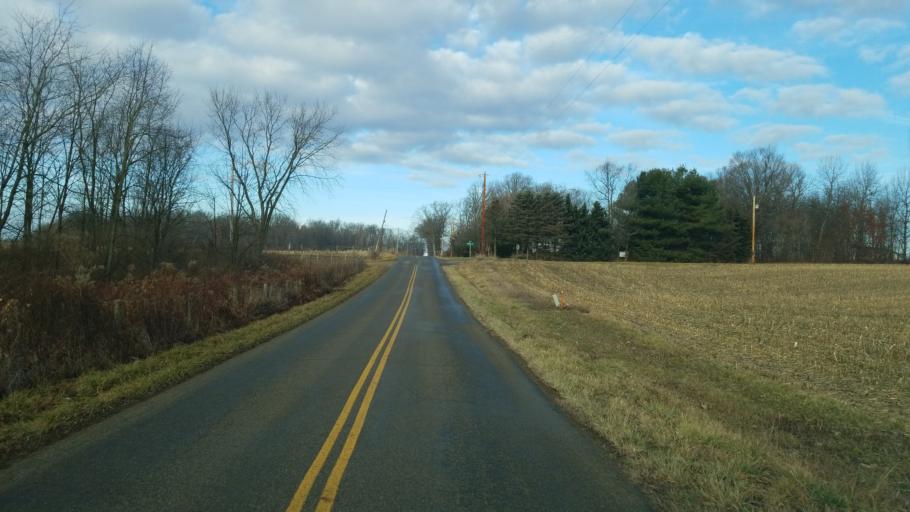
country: US
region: Ohio
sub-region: Knox County
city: Gambier
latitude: 40.3260
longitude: -82.3200
